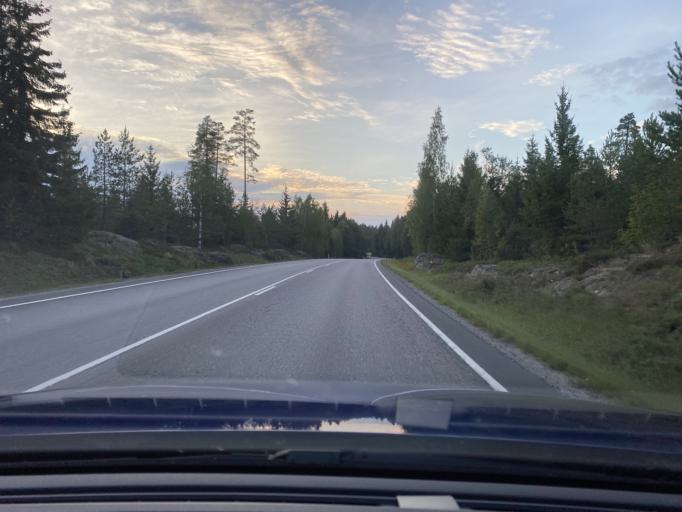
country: FI
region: Satakunta
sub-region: Pohjois-Satakunta
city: Kankaanpaeae
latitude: 61.7748
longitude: 22.4544
